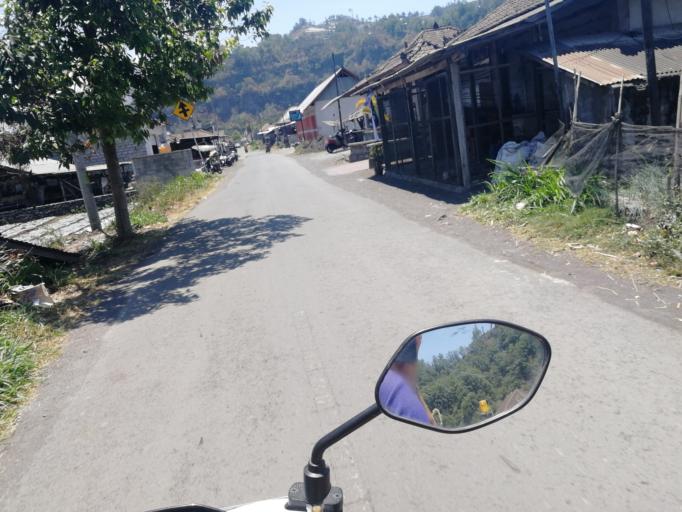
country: ID
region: Bali
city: Banjar Trunyan
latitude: -8.2224
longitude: 115.4147
